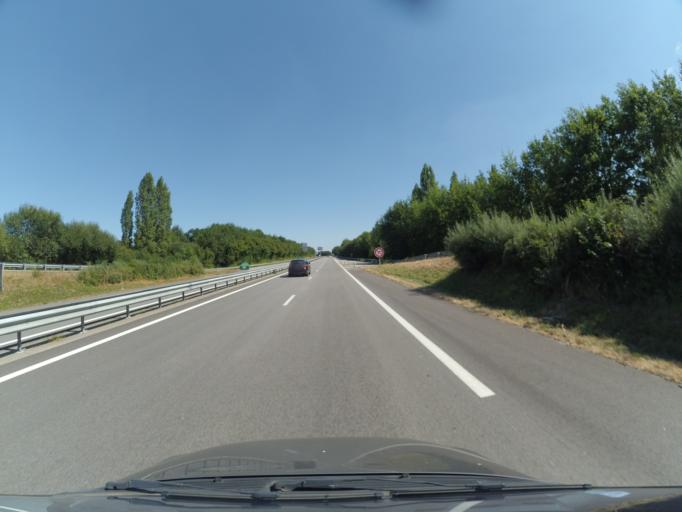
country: FR
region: Limousin
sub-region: Departement de la Haute-Vienne
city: Verneuil-sur-Vienne
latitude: 45.8537
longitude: 1.1574
